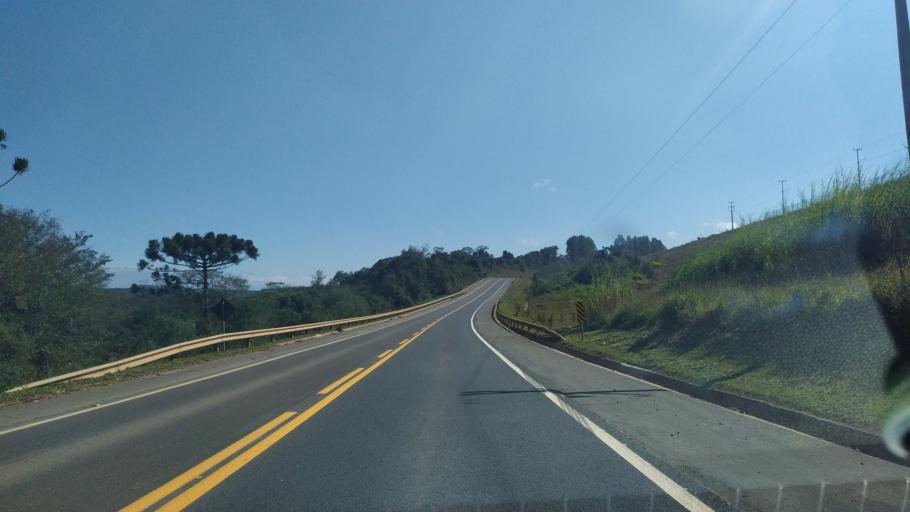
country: BR
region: Parana
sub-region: Telemaco Borba
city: Telemaco Borba
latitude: -24.2496
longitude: -50.7483
